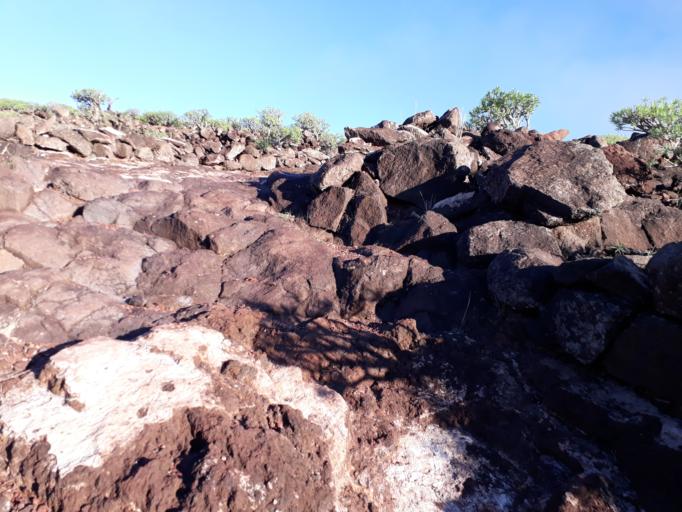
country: ES
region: Canary Islands
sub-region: Provincia de Santa Cruz de Tenerife
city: Vallehermosa
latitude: 28.1148
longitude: -17.3356
